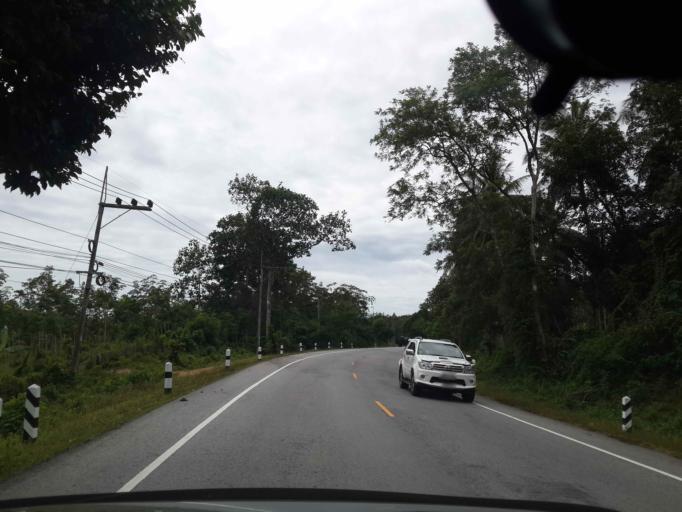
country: TH
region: Narathiwat
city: Rueso
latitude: 6.3579
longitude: 101.5594
